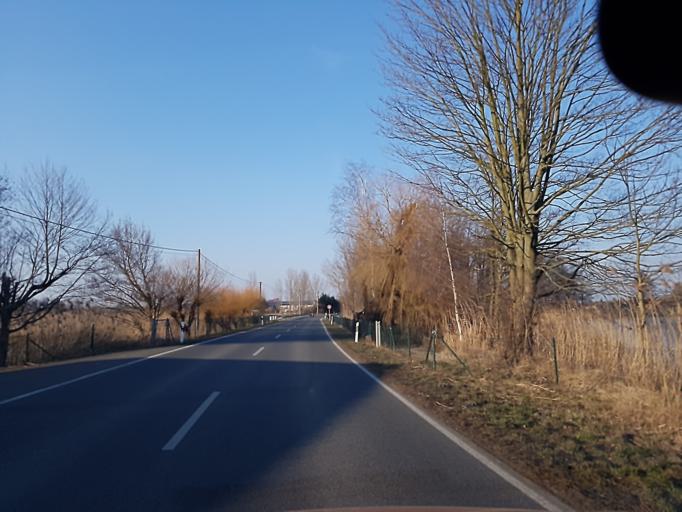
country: DE
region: Brandenburg
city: Ruckersdorf
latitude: 51.5991
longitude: 13.5515
